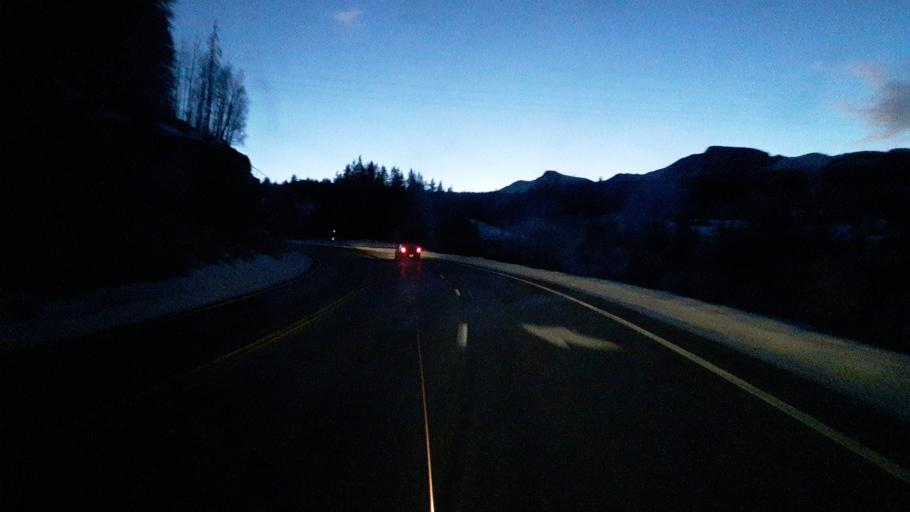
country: US
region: Colorado
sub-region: San Juan County
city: Silverton
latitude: 37.7264
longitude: -107.7371
